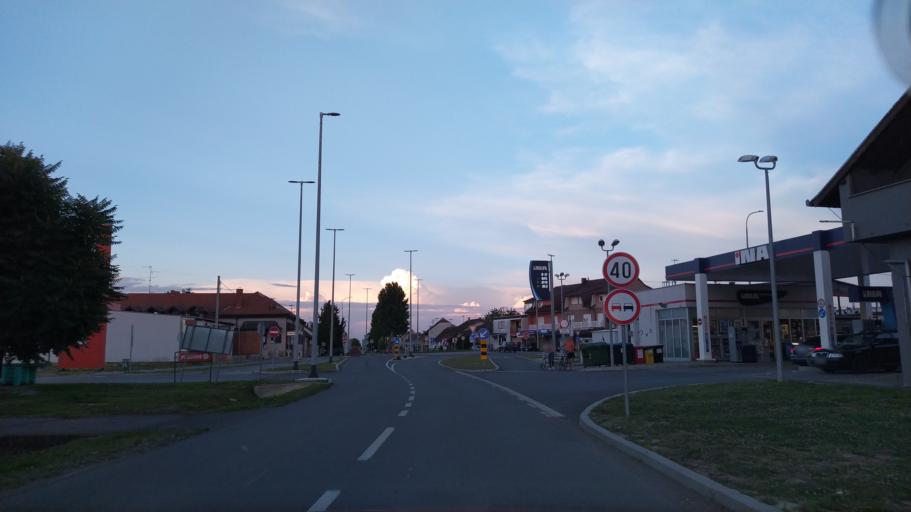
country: HR
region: Osjecko-Baranjska
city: Cepin
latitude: 45.5238
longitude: 18.5761
